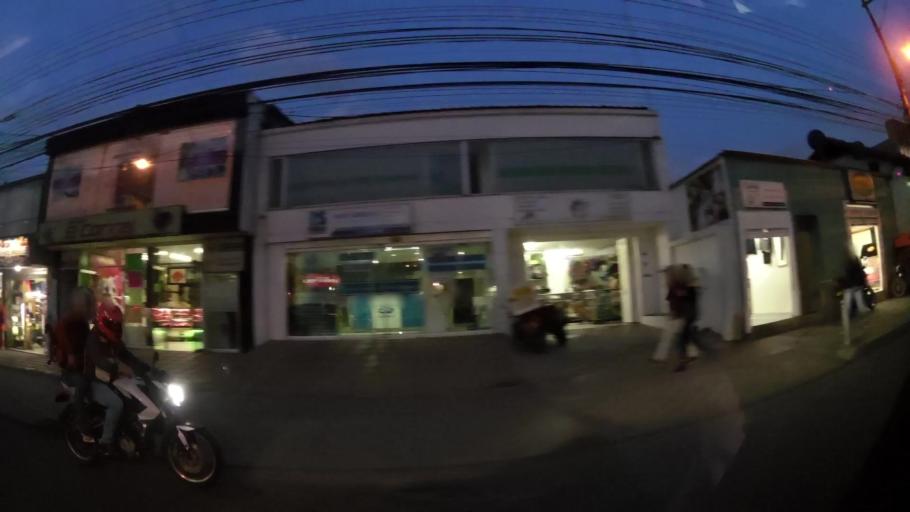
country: CO
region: Cundinamarca
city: Funza
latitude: 4.7169
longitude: -74.2114
